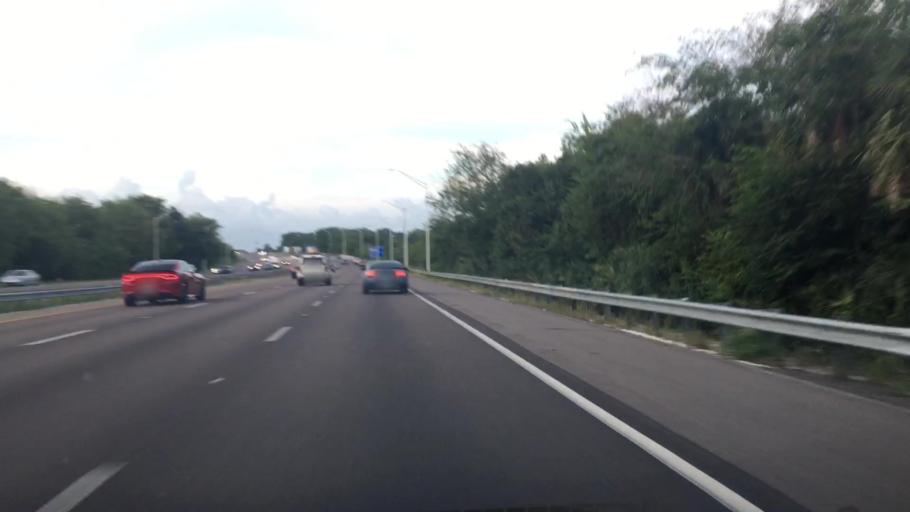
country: US
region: Florida
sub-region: Volusia County
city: DeBary
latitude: 28.8659
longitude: -81.2883
